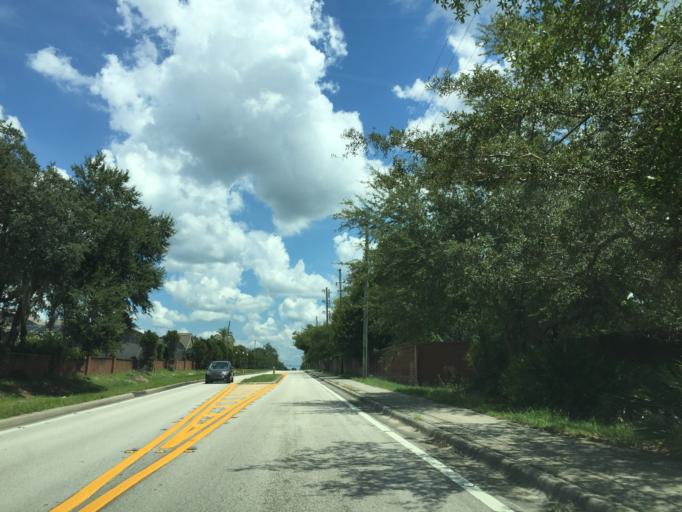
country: US
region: Florida
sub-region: Orange County
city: Alafaya
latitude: 28.6119
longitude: -81.2141
